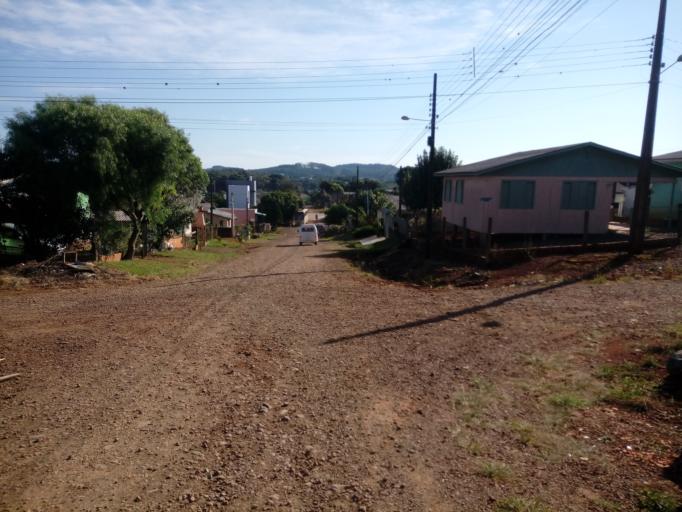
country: BR
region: Santa Catarina
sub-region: Chapeco
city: Chapeco
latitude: -27.0377
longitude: -52.6312
